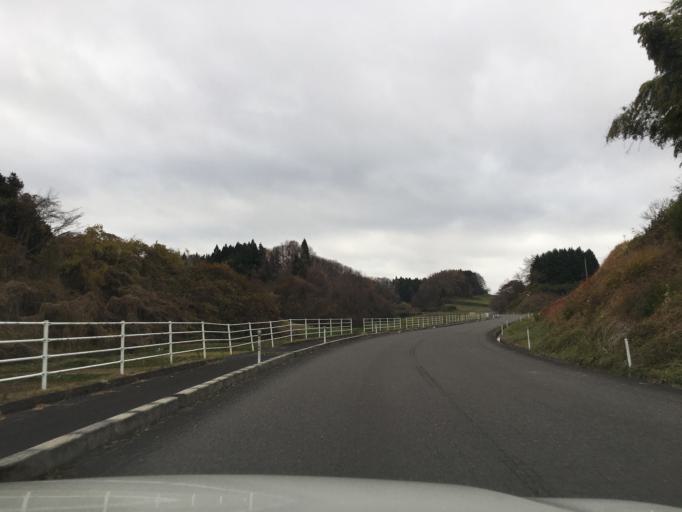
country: JP
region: Fukushima
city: Funehikimachi-funehiki
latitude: 37.4713
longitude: 140.5473
